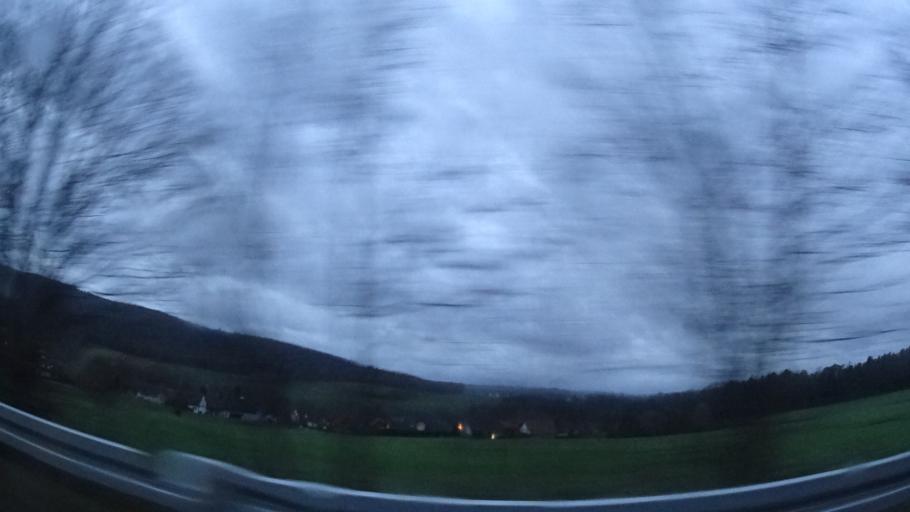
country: DE
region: Hesse
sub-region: Regierungsbezirk Kassel
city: Eichenzell
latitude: 50.4740
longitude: 9.6971
